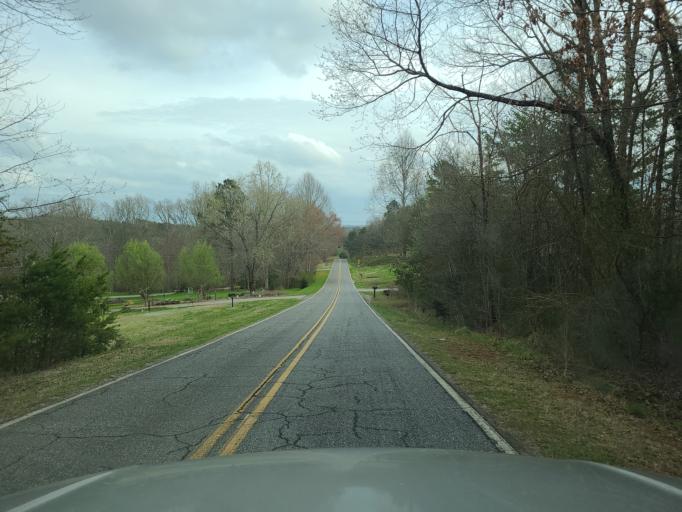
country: US
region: North Carolina
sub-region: Cleveland County
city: Boiling Springs
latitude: 35.2311
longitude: -81.7360
